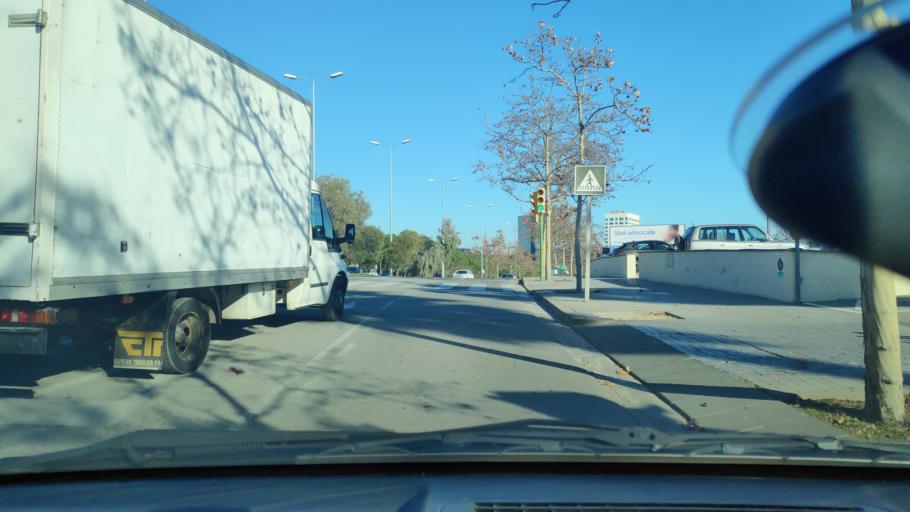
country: ES
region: Catalonia
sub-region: Provincia de Barcelona
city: Sabadell
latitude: 41.5502
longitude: 2.0925
